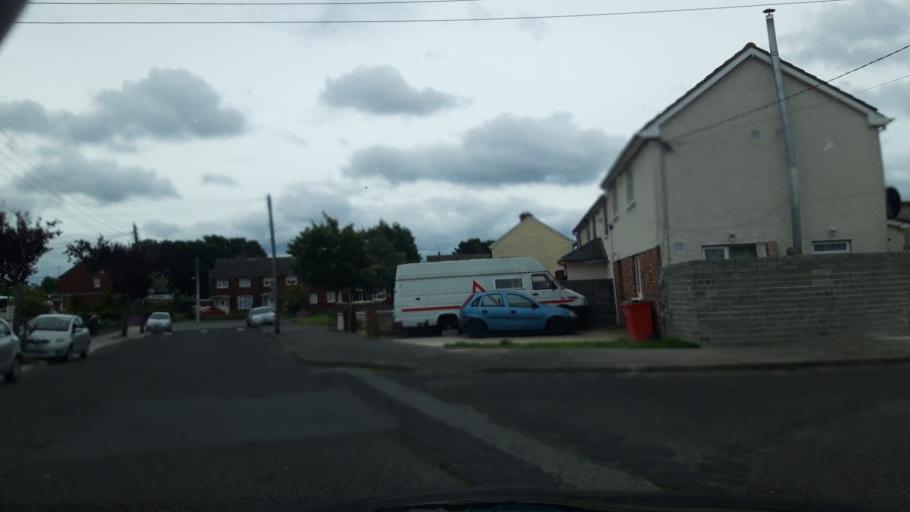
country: IE
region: Leinster
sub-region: Dublin City
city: Finglas
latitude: 53.3849
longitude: -6.3051
